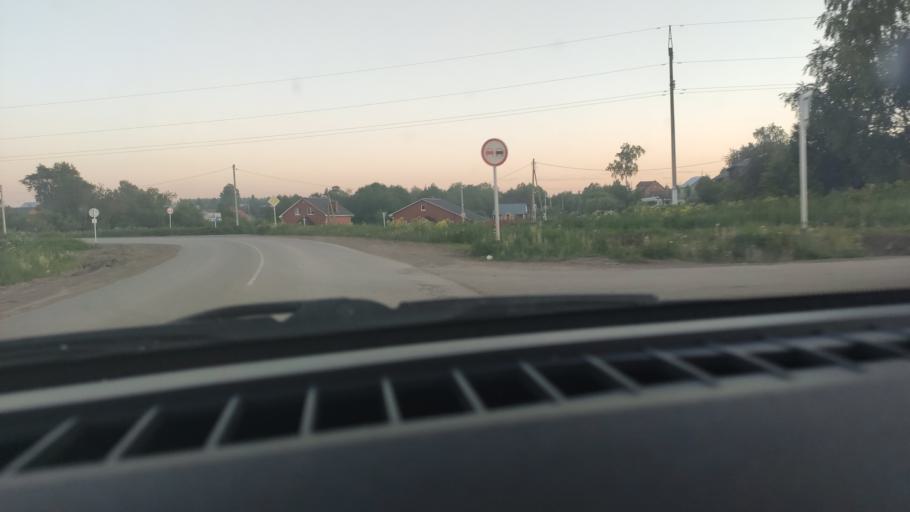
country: RU
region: Perm
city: Kultayevo
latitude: 57.8954
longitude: 55.9150
